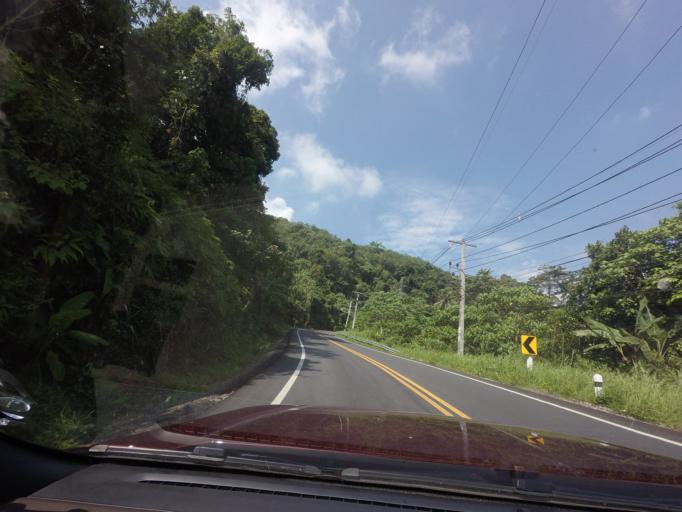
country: TH
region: Yala
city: Betong
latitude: 5.9114
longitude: 101.1545
